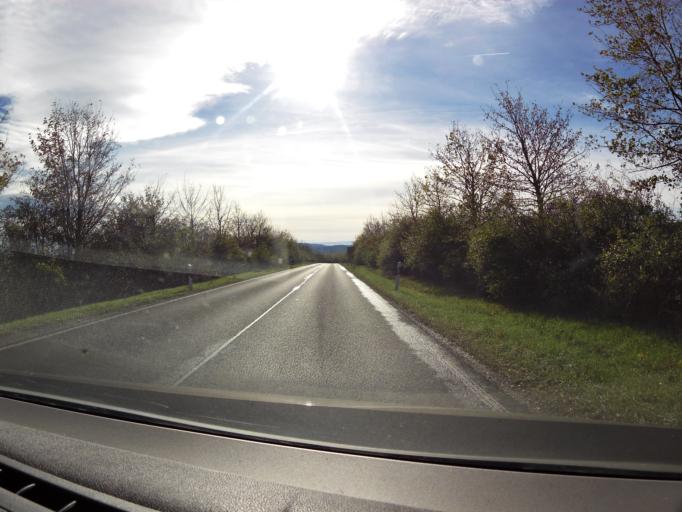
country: DE
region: Thuringia
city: Crawinkel
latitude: 50.7755
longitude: 10.7908
